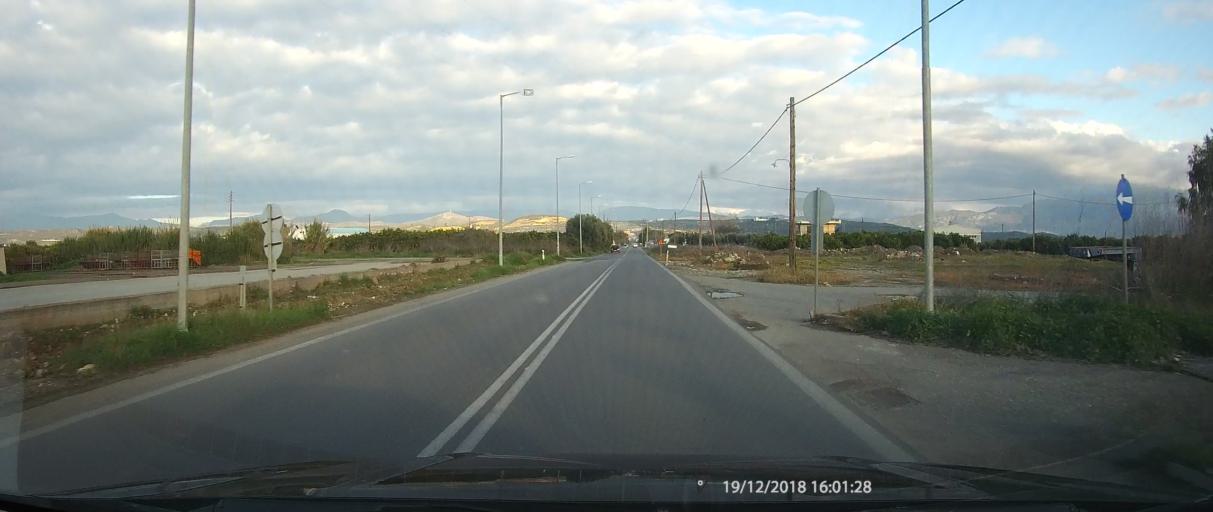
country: GR
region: Peloponnese
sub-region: Nomos Lakonias
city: Vlakhiotis
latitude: 36.8568
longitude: 22.6884
